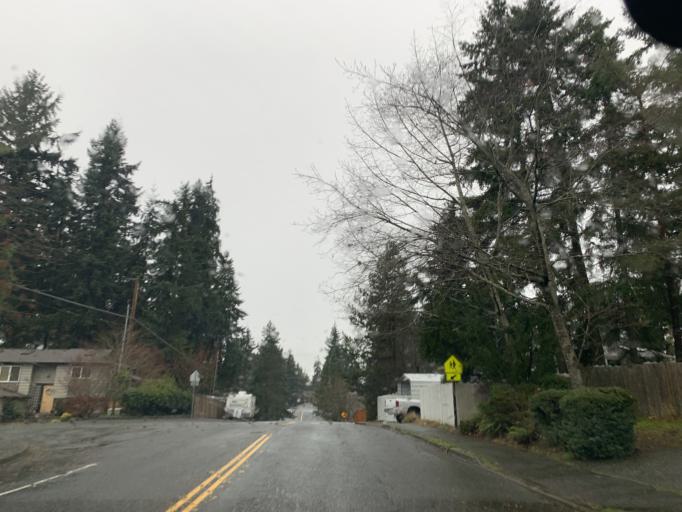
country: US
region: Washington
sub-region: King County
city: Kingsgate
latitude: 47.7258
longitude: -122.1724
